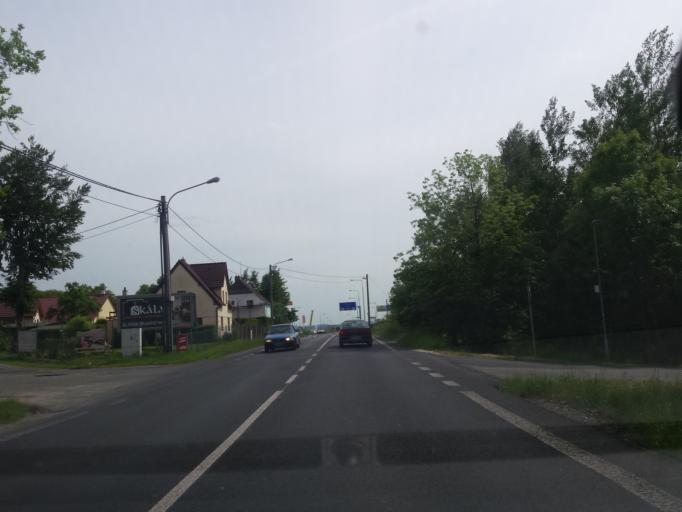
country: CZ
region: Liberecky
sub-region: Okres Ceska Lipa
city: Ceska Lipa
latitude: 50.7029
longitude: 14.5430
